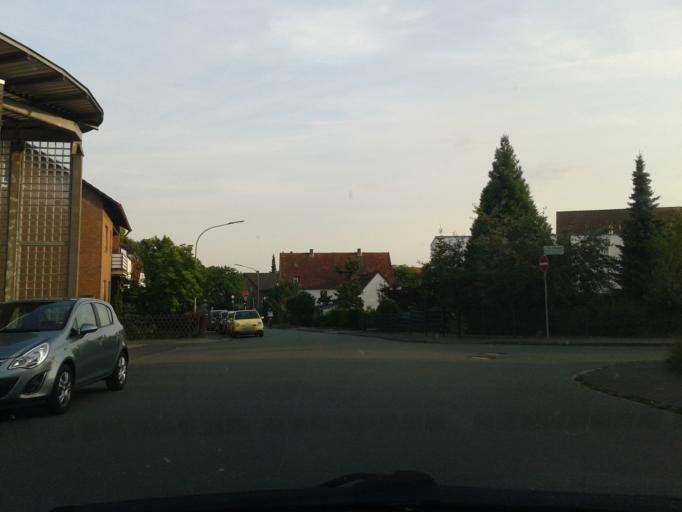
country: DE
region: North Rhine-Westphalia
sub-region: Regierungsbezirk Detmold
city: Paderborn
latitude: 51.7329
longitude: 8.6852
